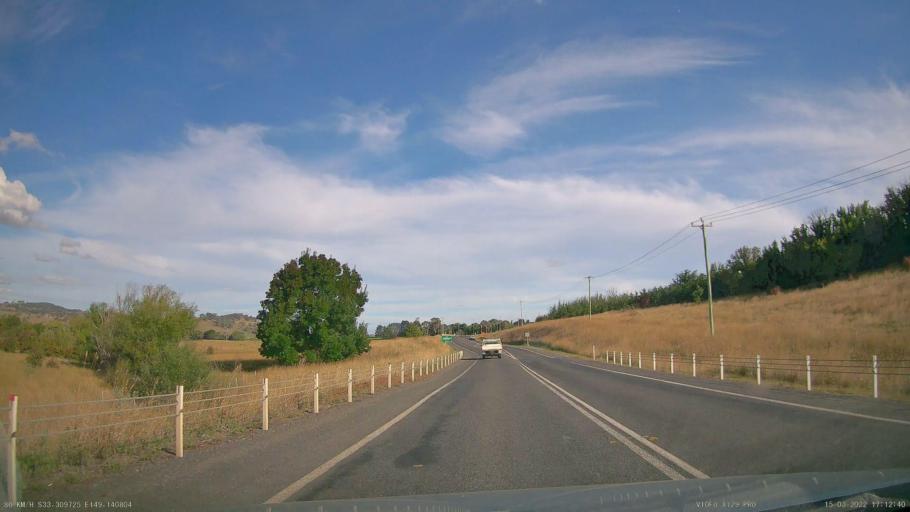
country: AU
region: New South Wales
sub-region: Orange Municipality
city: Orange
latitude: -33.3099
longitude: 149.1409
